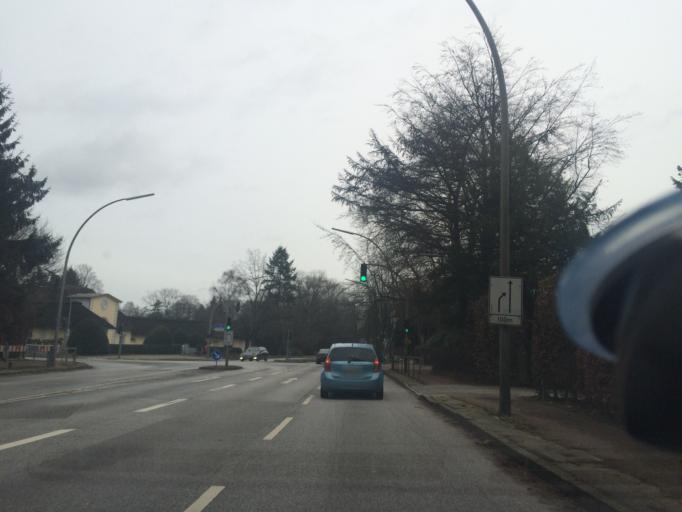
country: DE
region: Hamburg
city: Altona
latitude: 53.5465
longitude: 9.8889
